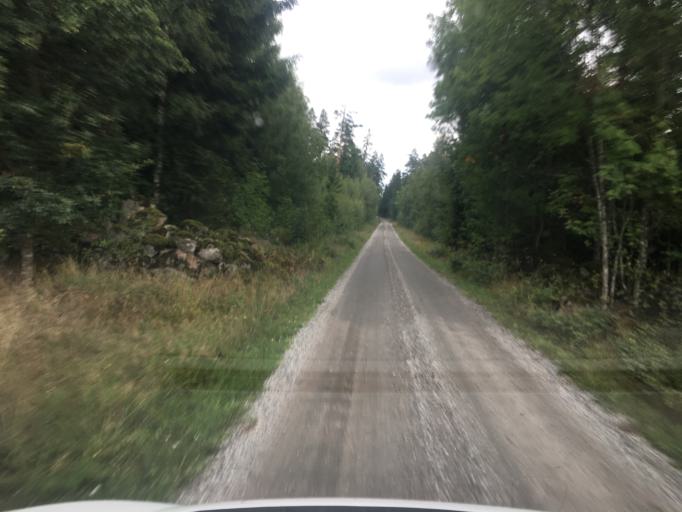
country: SE
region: Kronoberg
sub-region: Ljungby Kommun
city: Lagan
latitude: 56.9579
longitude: 14.0424
